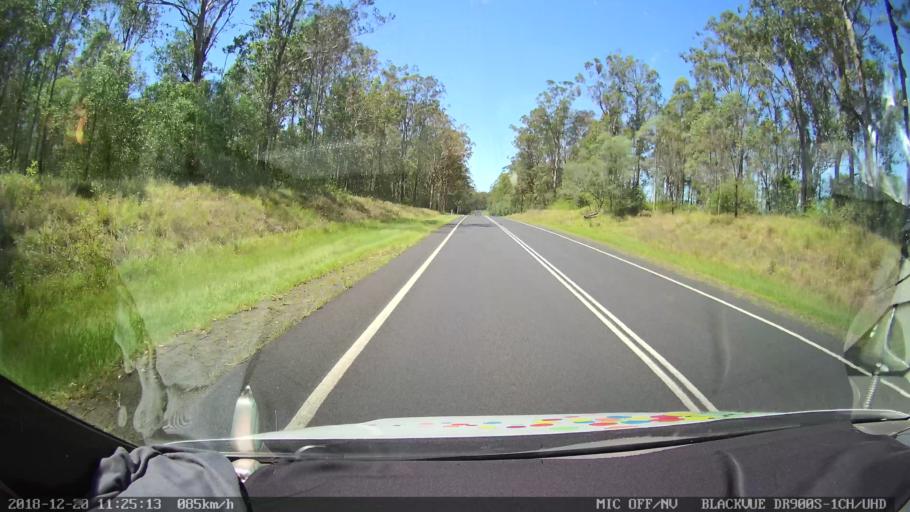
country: AU
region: New South Wales
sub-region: Richmond Valley
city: Casino
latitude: -29.0846
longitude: 153.0007
